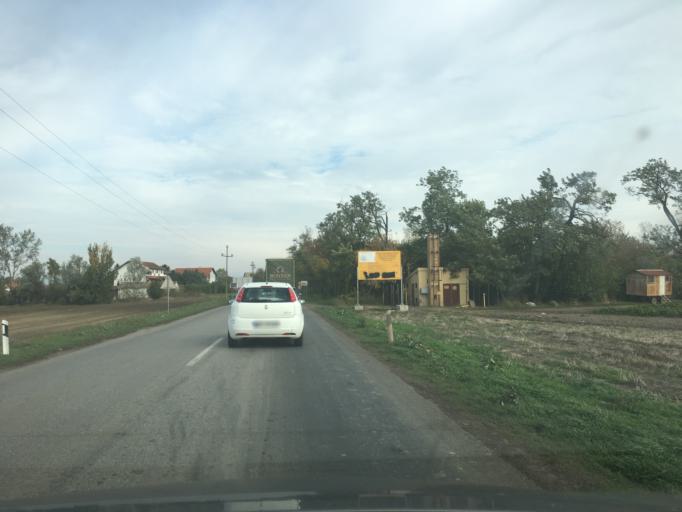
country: RS
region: Autonomna Pokrajina Vojvodina
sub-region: Juznobacki Okrug
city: Zabalj
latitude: 45.3573
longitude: 20.0650
